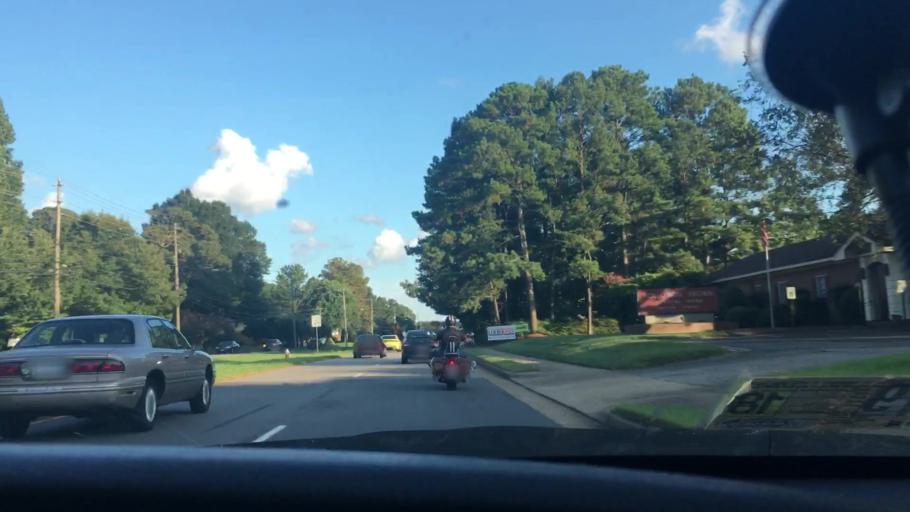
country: US
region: Virginia
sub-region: City of Norfolk
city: Norfolk
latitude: 36.8878
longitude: -76.1369
